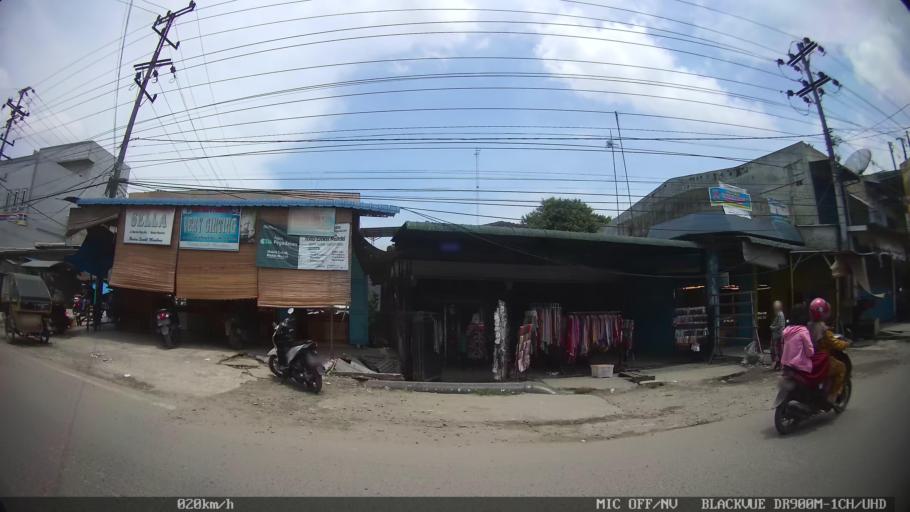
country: ID
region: North Sumatra
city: Labuhan Deli
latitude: 3.7096
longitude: 98.6604
